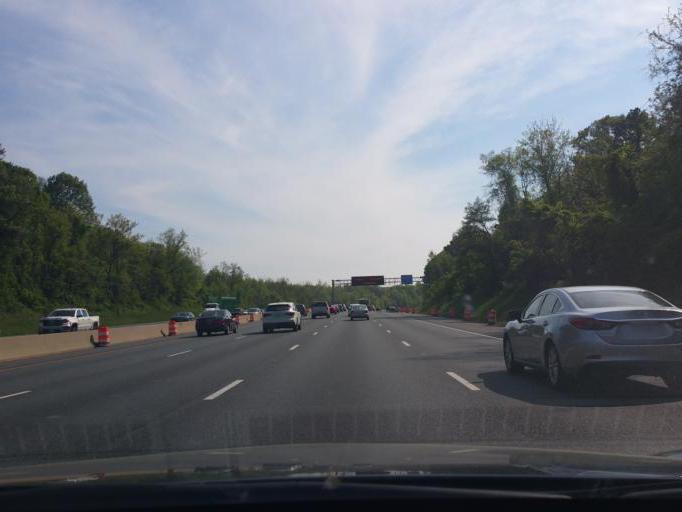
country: US
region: Maryland
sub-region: Baltimore County
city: Kingsville
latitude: 39.4144
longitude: -76.4106
